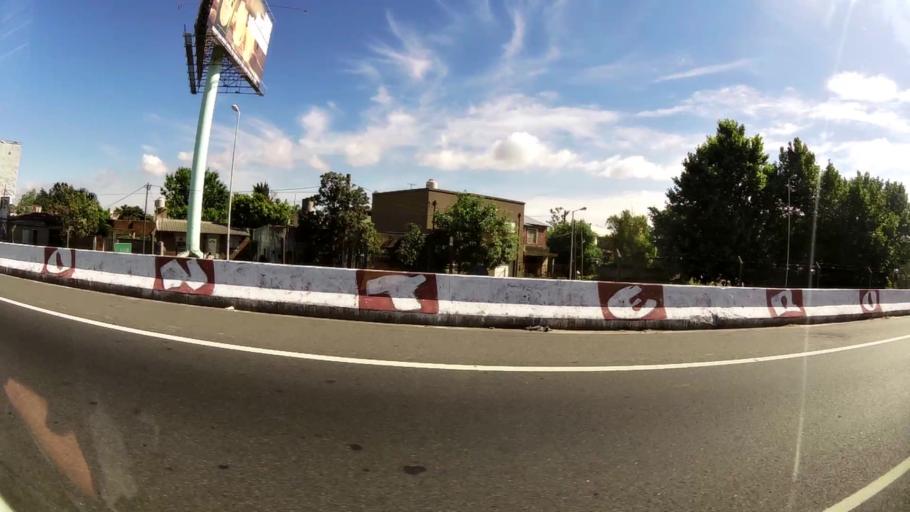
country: AR
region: Buenos Aires
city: Caseros
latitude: -34.6310
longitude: -58.5781
